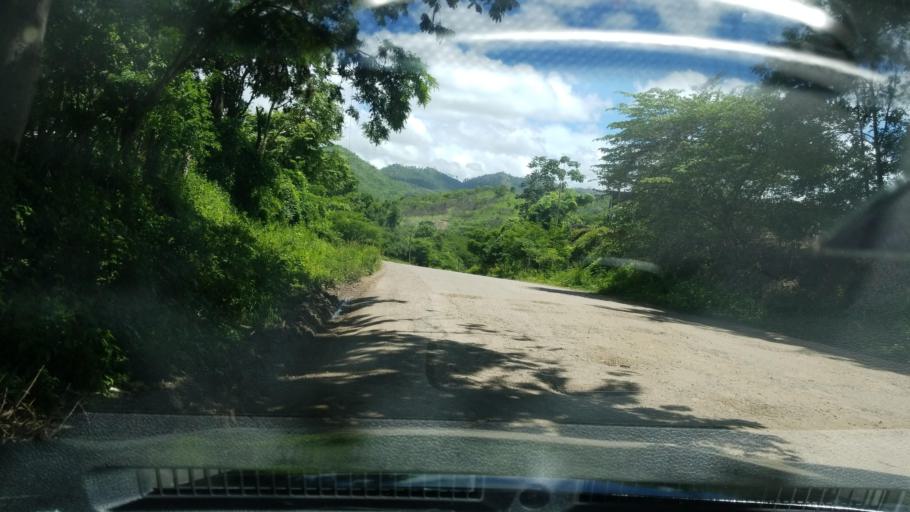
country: HN
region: Francisco Morazan
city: San Juan de Flores
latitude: 14.3132
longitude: -87.0383
